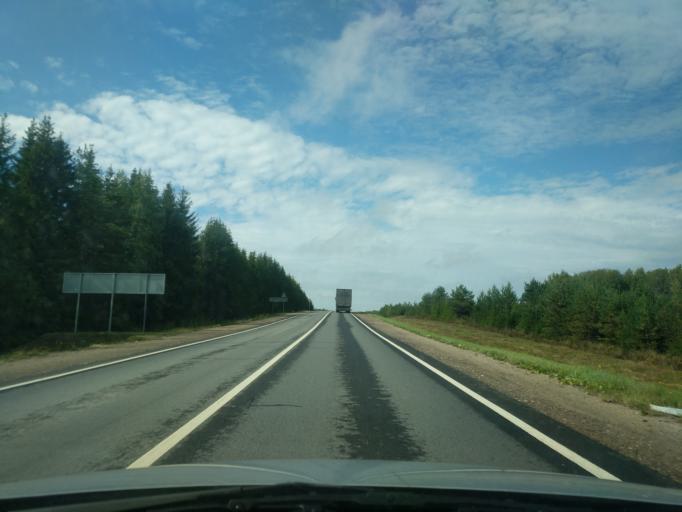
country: RU
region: Kostroma
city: Sudislavl'
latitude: 57.8417
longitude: 41.8400
